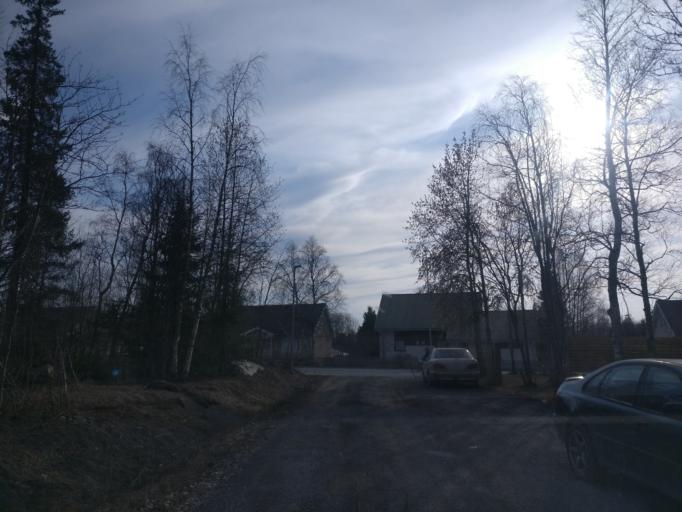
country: FI
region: Lapland
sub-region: Kemi-Tornio
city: Kemi
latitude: 65.7322
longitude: 24.5985
